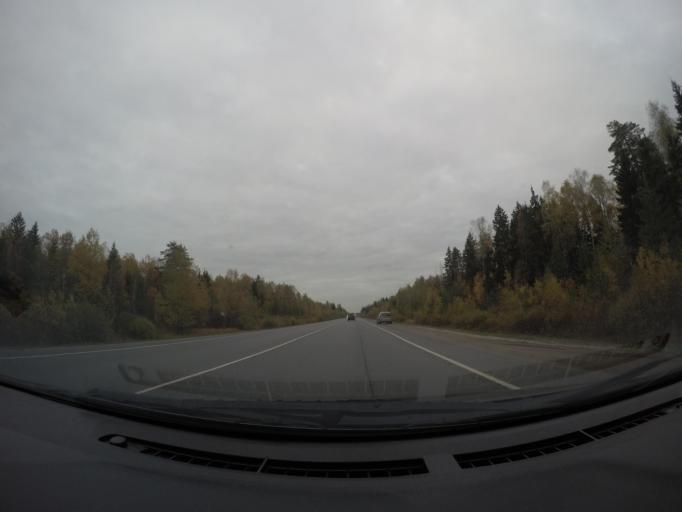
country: RU
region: Moskovskaya
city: Fryazevo
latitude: 55.7127
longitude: 38.4257
